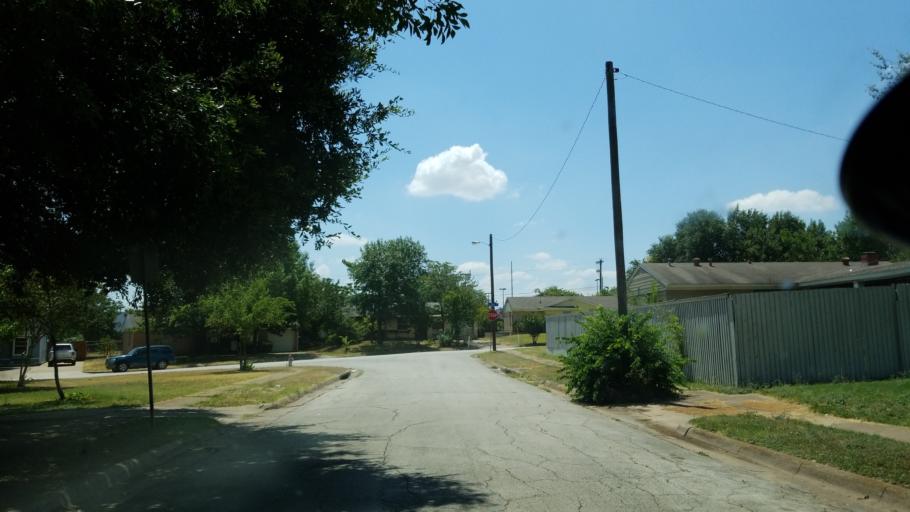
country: US
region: Texas
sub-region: Dallas County
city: Duncanville
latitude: 32.6647
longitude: -96.8930
